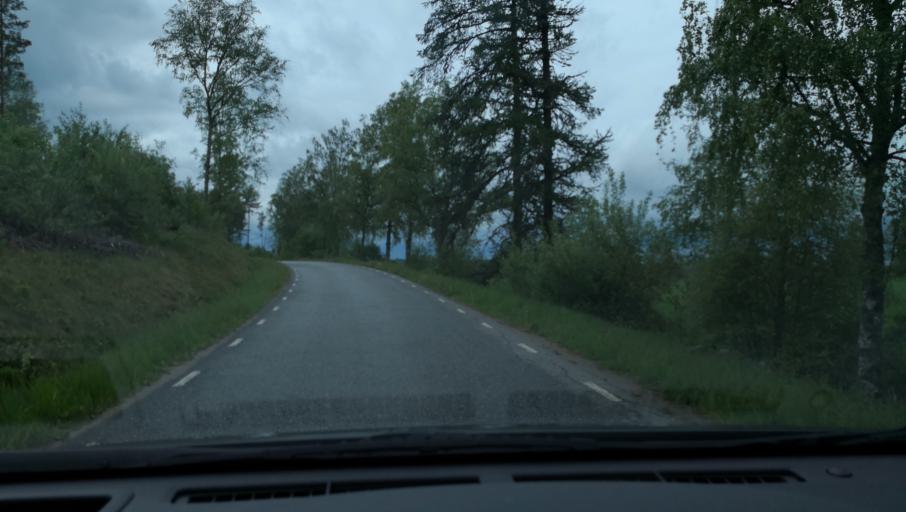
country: SE
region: Uppsala
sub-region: Enkopings Kommun
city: Orsundsbro
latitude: 59.7242
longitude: 17.3814
